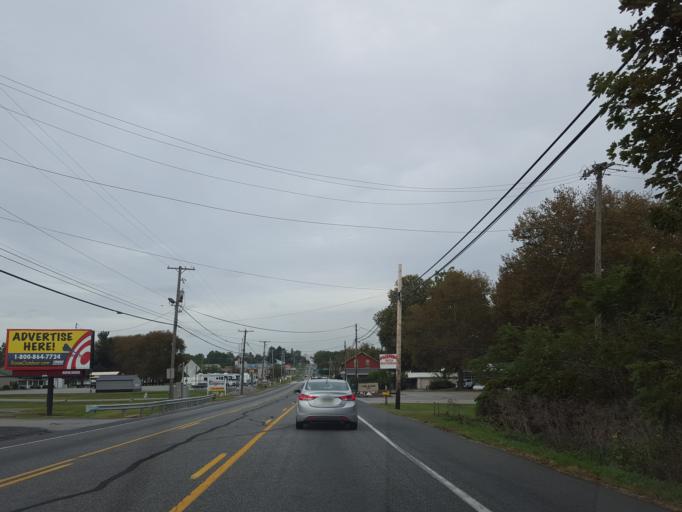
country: US
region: Pennsylvania
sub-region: York County
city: Weigelstown
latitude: 39.9286
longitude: -76.8335
